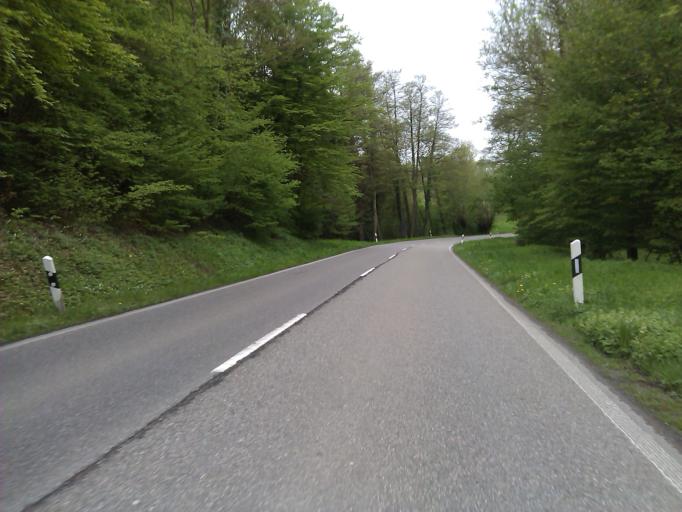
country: DE
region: Baden-Wuerttemberg
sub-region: Karlsruhe Region
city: Oberderdingen
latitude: 49.0549
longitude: 8.8203
